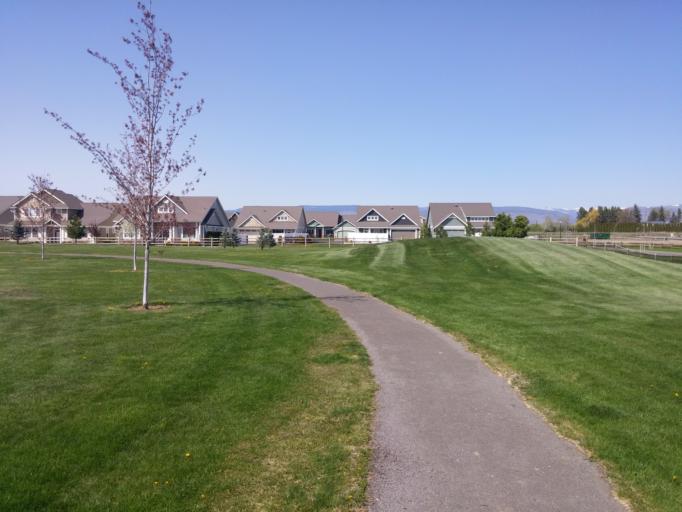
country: US
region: Washington
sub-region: Kittitas County
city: Ellensburg
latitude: 47.0164
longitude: -120.5295
